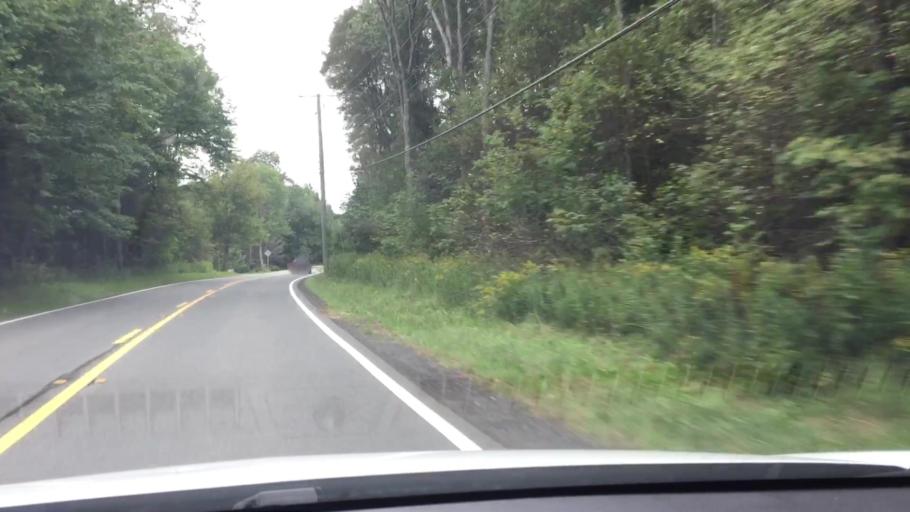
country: US
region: Massachusetts
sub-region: Berkshire County
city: Hinsdale
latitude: 42.3873
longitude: -73.1232
